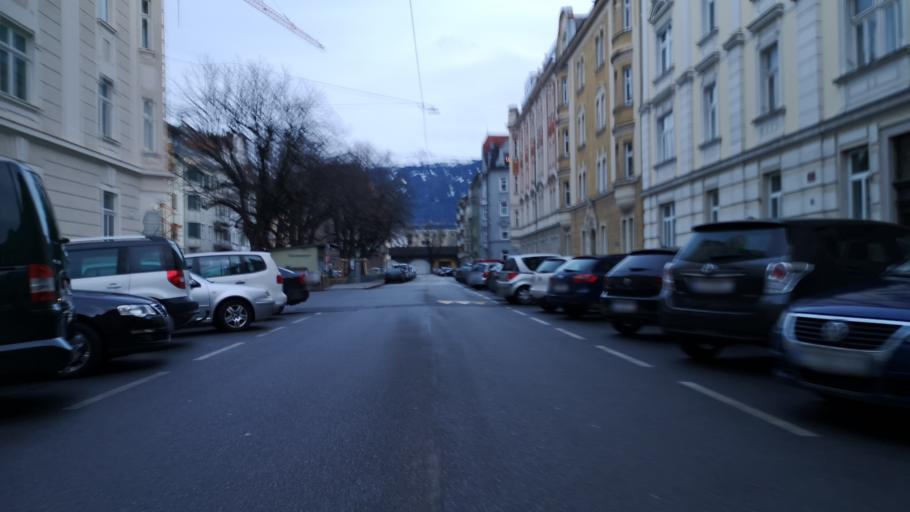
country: AT
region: Tyrol
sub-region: Innsbruck Stadt
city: Innsbruck
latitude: 47.2754
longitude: 11.4060
